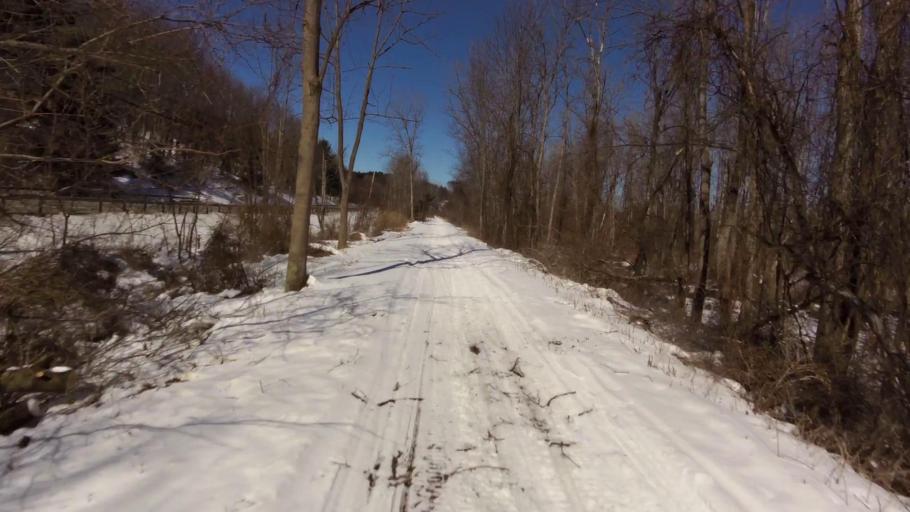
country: US
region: New York
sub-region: Allegany County
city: Houghton
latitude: 42.3774
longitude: -78.1495
